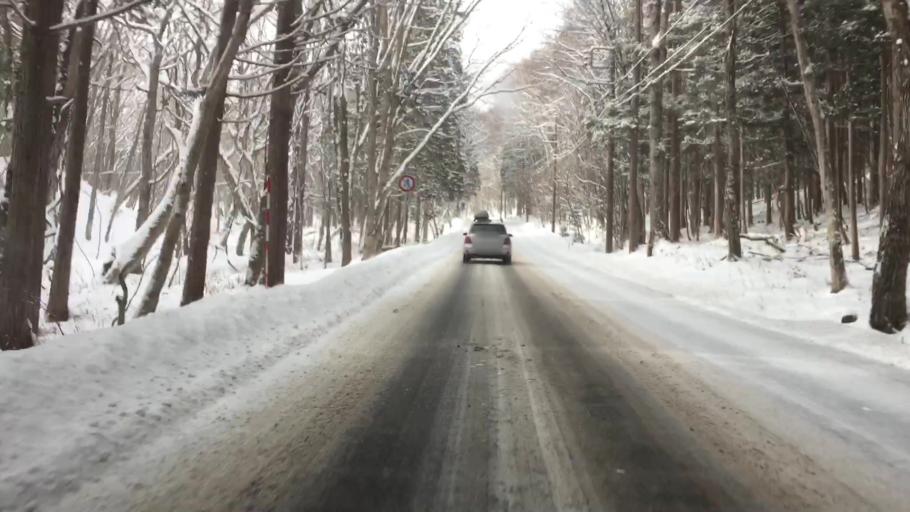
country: JP
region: Tochigi
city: Yaita
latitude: 36.9533
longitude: 139.7600
